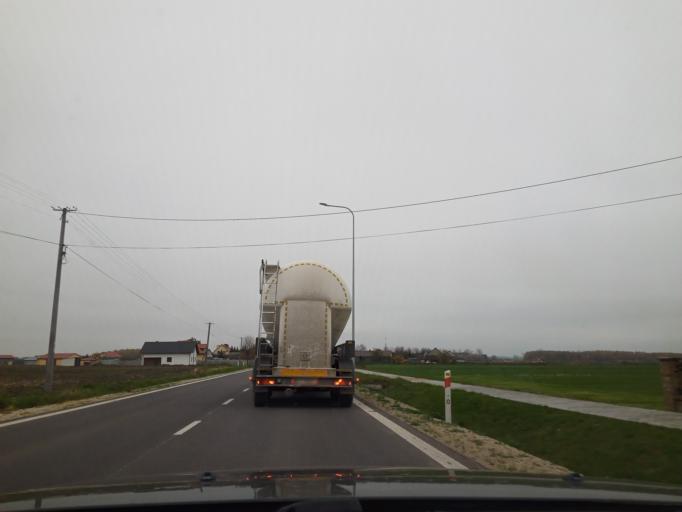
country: PL
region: Swietokrzyskie
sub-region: Powiat jedrzejowski
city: Jedrzejow
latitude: 50.6000
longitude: 20.3200
